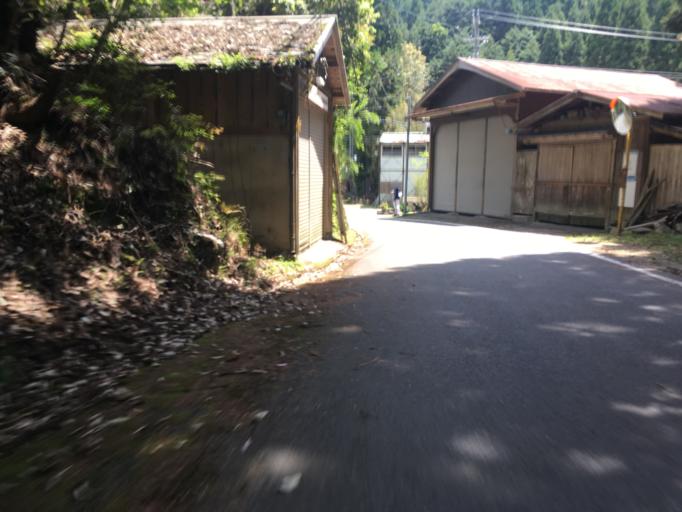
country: JP
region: Kyoto
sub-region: Kyoto-shi
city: Kamigyo-ku
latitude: 35.1142
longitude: 135.7149
